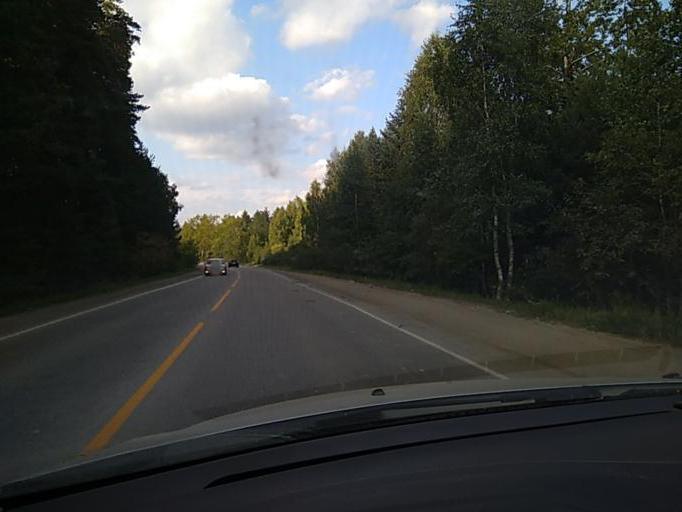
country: RU
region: Chelyabinsk
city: Kyshtym
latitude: 55.6803
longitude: 60.5628
